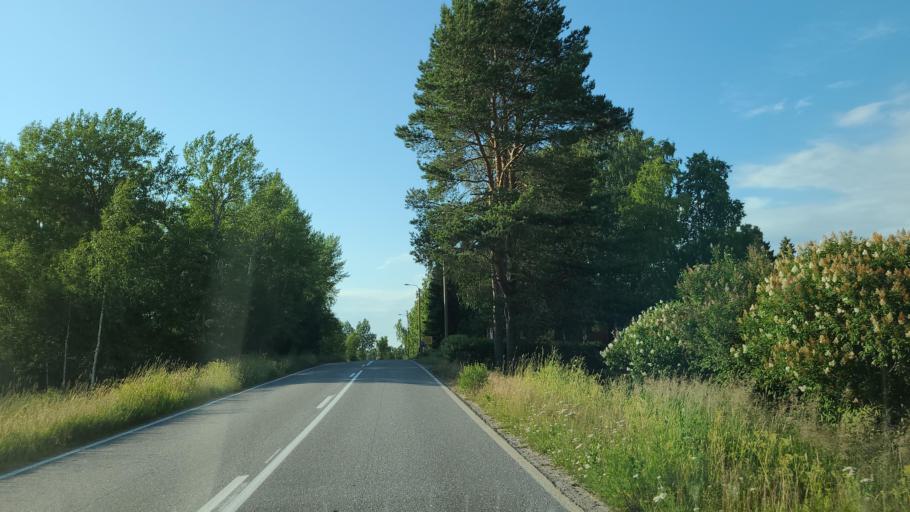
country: FI
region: Ostrobothnia
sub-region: Vaasa
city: Replot
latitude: 63.3350
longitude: 21.3339
